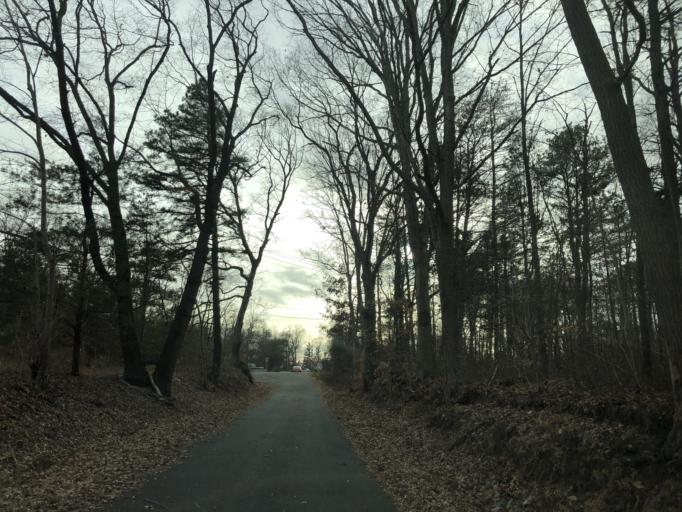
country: US
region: Maryland
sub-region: Cecil County
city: North East
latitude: 39.6048
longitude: -75.9596
